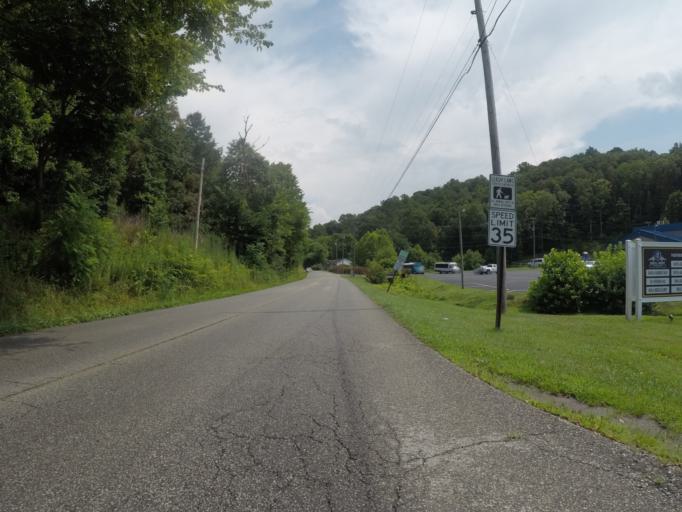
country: US
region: Kentucky
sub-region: Boyd County
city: Ironville
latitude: 38.4568
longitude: -82.6774
